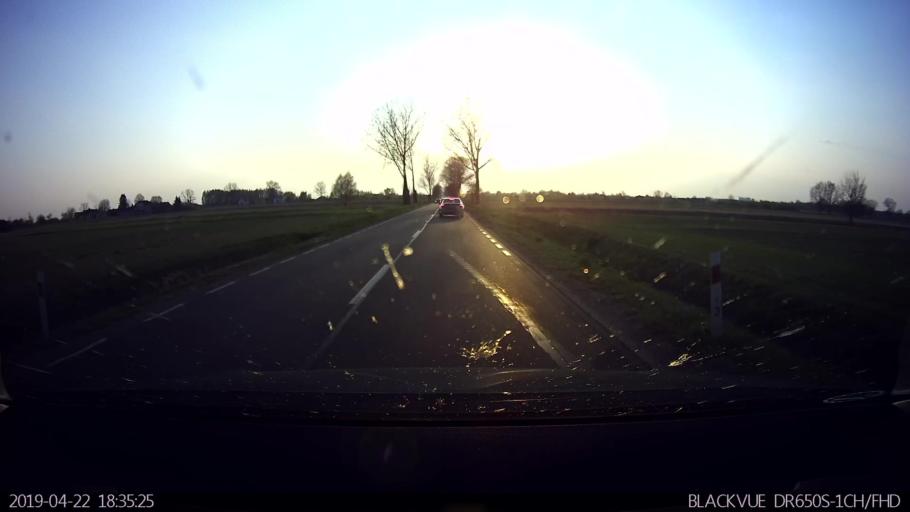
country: PL
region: Masovian Voivodeship
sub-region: Powiat wolominski
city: Klembow
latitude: 52.4455
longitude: 21.3505
